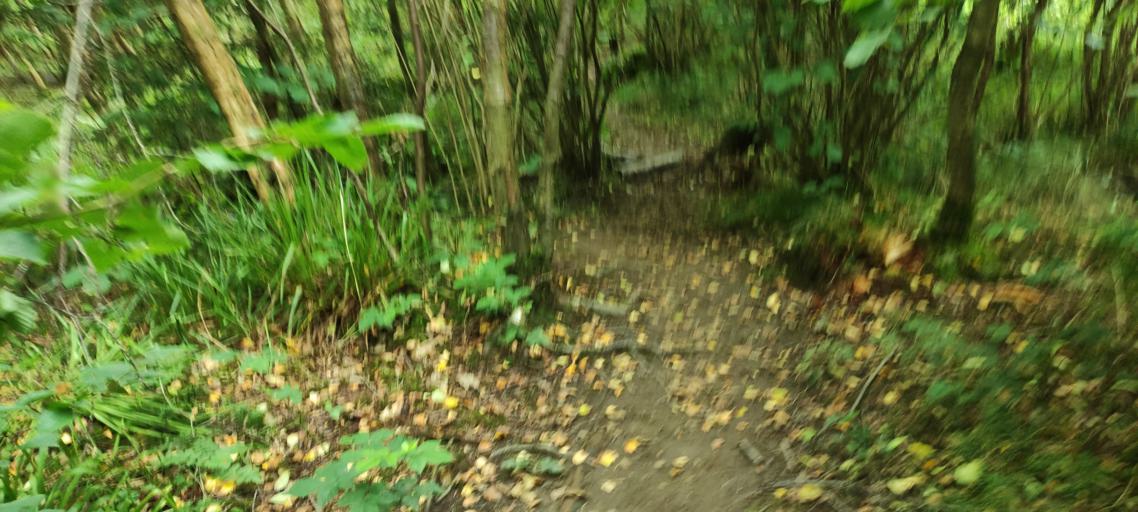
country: GB
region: England
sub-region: Cumbria
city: Wigton
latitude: 54.7497
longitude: -3.0378
